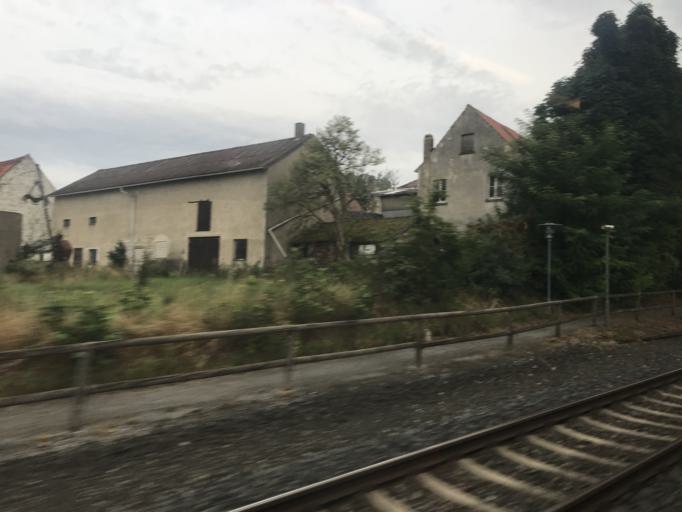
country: DE
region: Bavaria
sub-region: Regierungsbezirk Unterfranken
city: Oberpleichfeld
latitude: 49.8563
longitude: 10.1021
